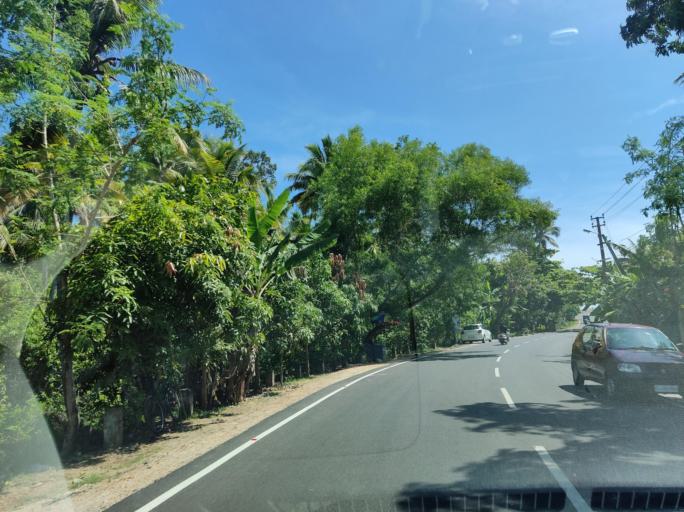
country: IN
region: Kerala
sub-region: Alappuzha
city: Kayankulam
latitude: 9.1696
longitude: 76.4598
